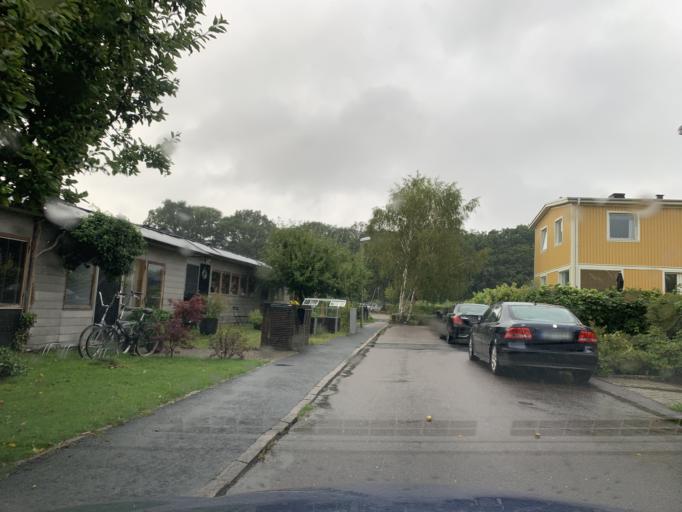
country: SE
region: Vaestra Goetaland
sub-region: Goteborg
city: Goeteborg
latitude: 57.7040
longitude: 12.0123
